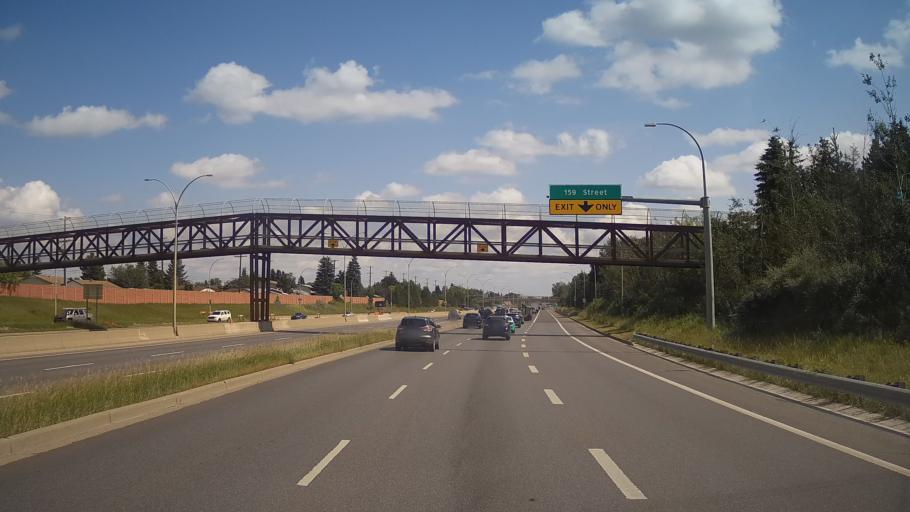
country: CA
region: Alberta
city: St. Albert
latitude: 53.5114
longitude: -113.6116
